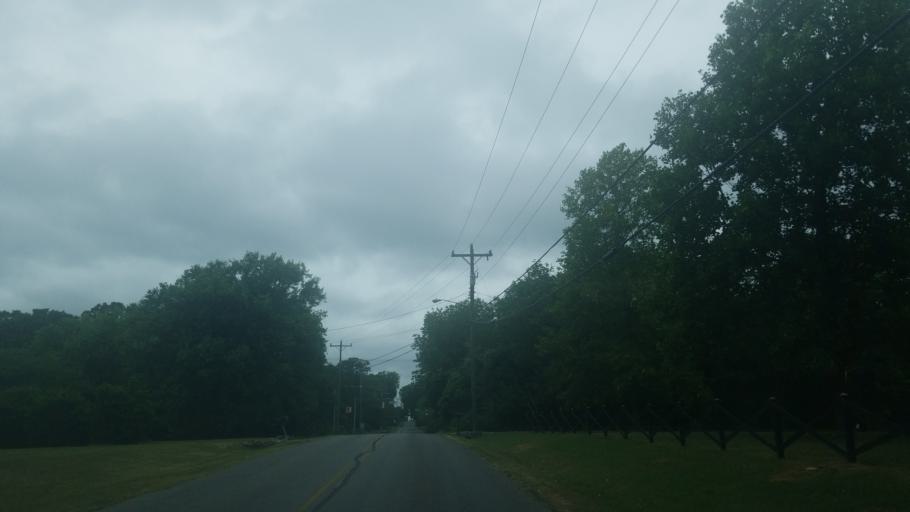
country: US
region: Tennessee
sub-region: Rutherford County
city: La Vergne
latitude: 36.0491
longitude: -86.5984
